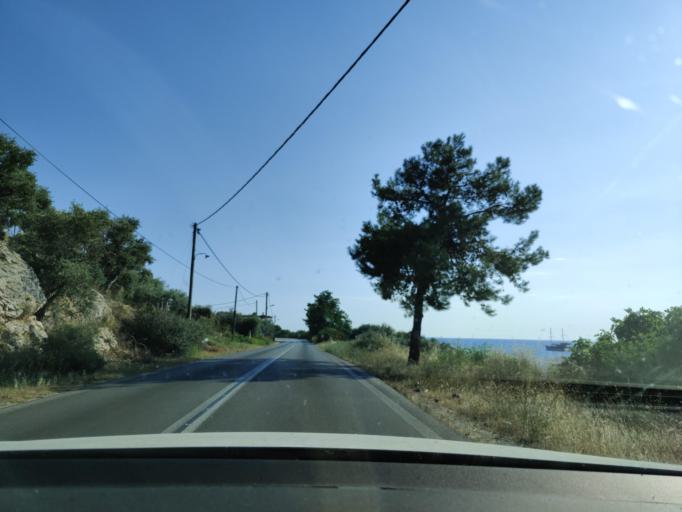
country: GR
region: East Macedonia and Thrace
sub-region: Nomos Kavalas
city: Prinos
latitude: 40.7156
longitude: 24.5362
